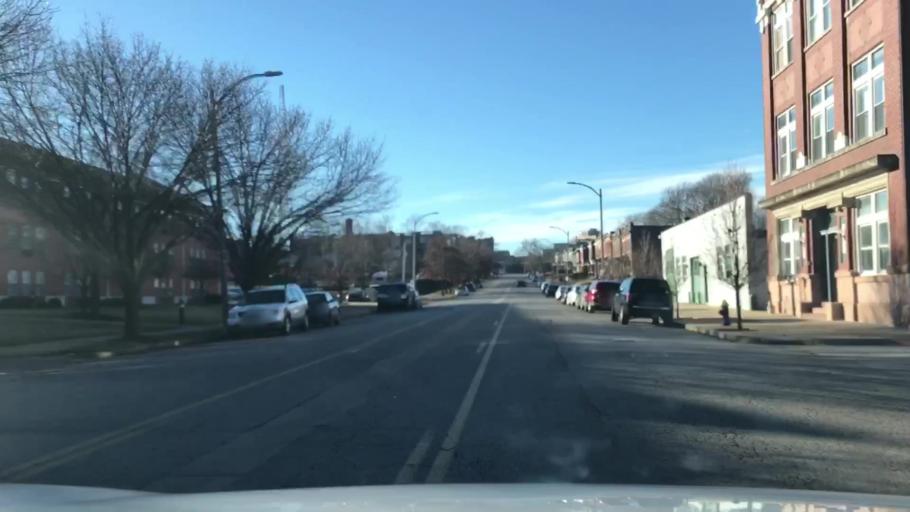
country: US
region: Missouri
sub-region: City of Saint Louis
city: St. Louis
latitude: 38.6200
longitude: -90.2328
